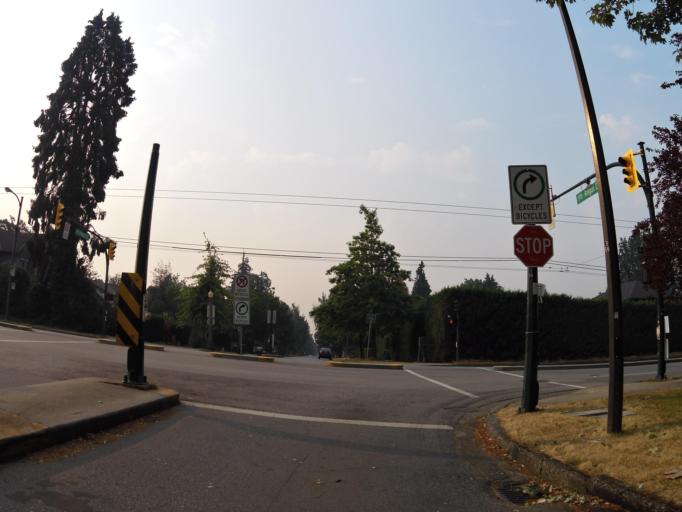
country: CA
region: British Columbia
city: Vancouver
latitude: 49.2346
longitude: -123.1477
